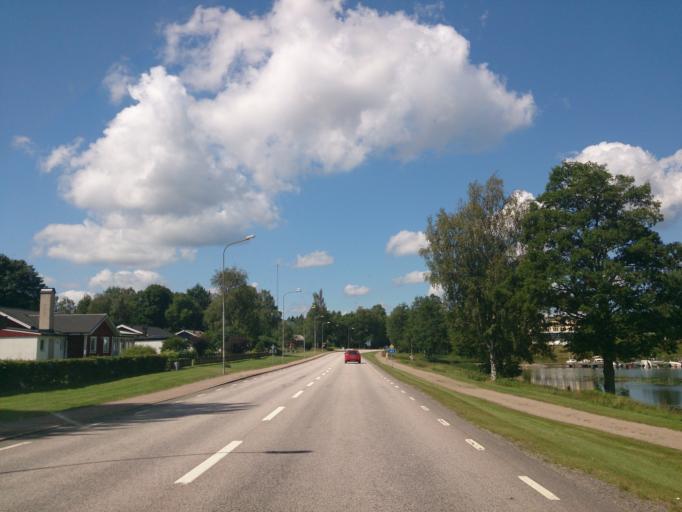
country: SE
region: Halland
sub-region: Hylte Kommun
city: Torup
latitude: 57.1058
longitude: 13.0356
